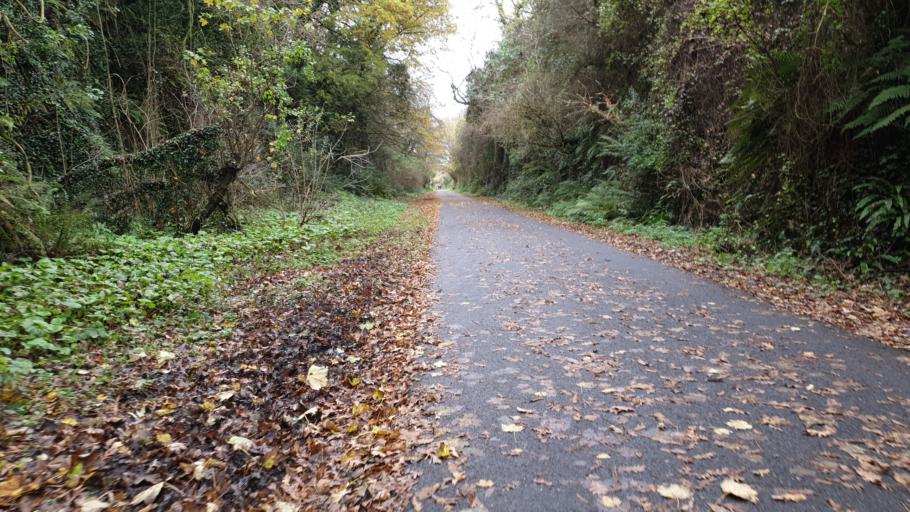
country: IE
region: Munster
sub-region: County Cork
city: Cork
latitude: 51.8884
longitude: -8.4098
